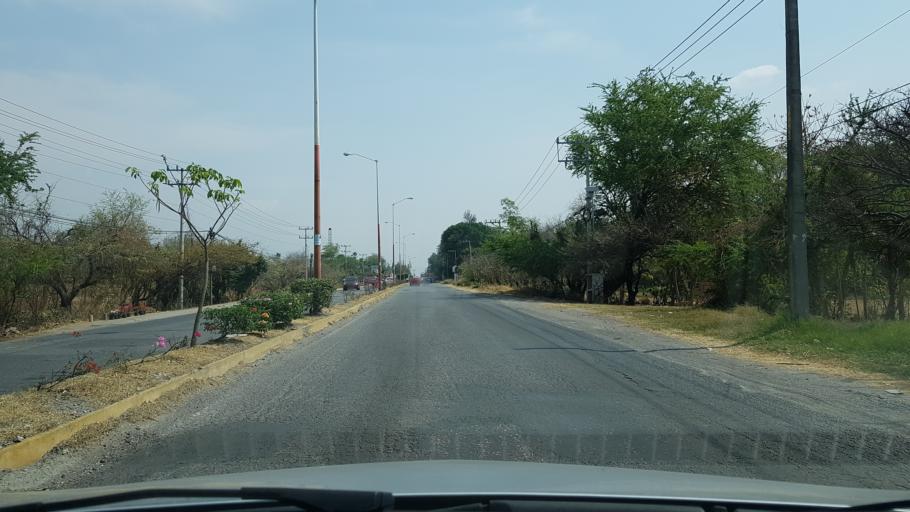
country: MX
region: Morelos
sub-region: Xochitepec
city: Chiconcuac
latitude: 18.7862
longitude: -99.2050
